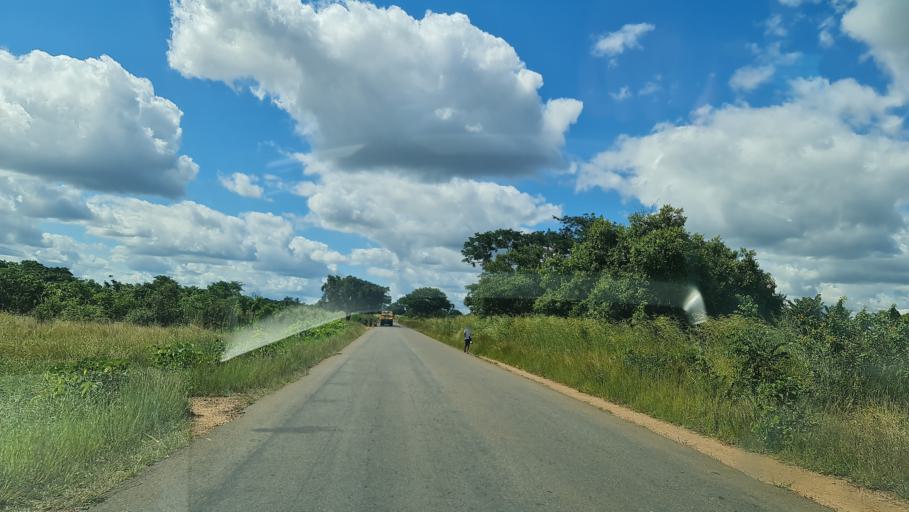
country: MZ
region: Zambezia
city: Quelimane
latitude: -17.5139
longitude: 36.2238
